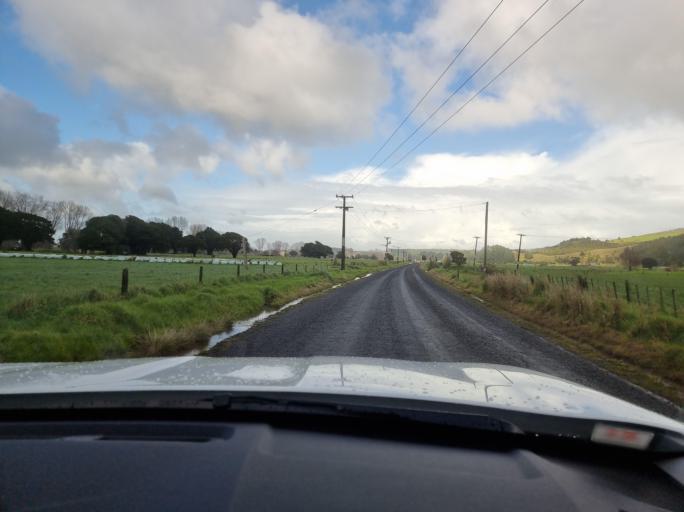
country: NZ
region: Northland
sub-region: Kaipara District
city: Dargaville
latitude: -35.7937
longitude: 173.7304
